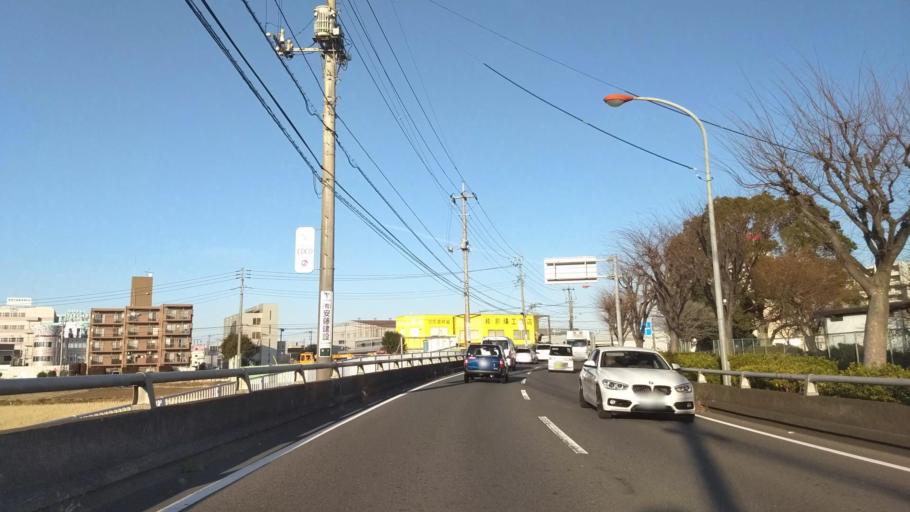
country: JP
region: Kanagawa
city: Atsugi
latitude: 35.4266
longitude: 139.3560
